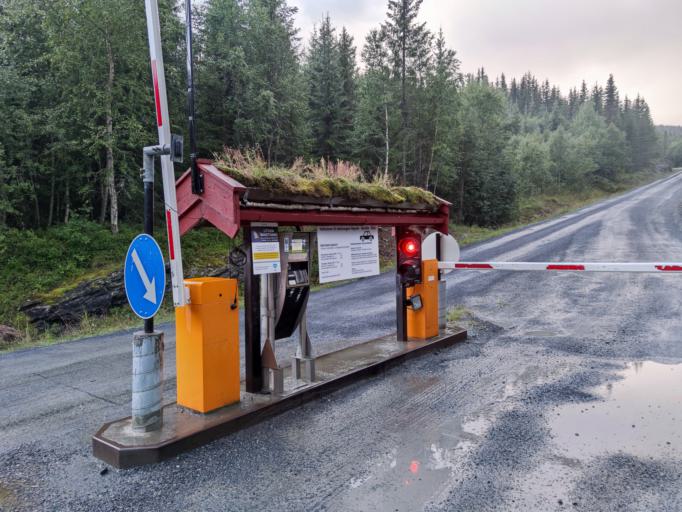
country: NO
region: Oppland
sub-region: Vestre Slidre
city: Slidre
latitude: 61.1215
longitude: 8.8248
